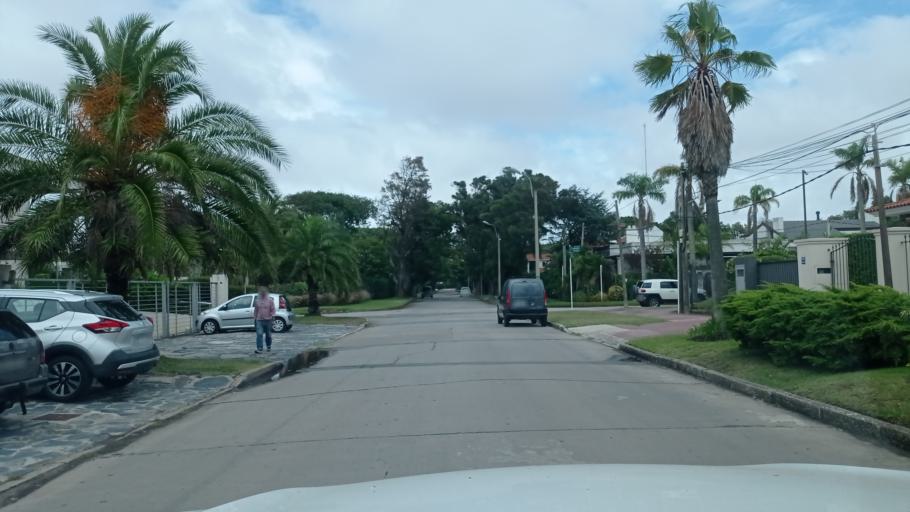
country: UY
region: Canelones
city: Barra de Carrasco
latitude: -34.8873
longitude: -56.0504
